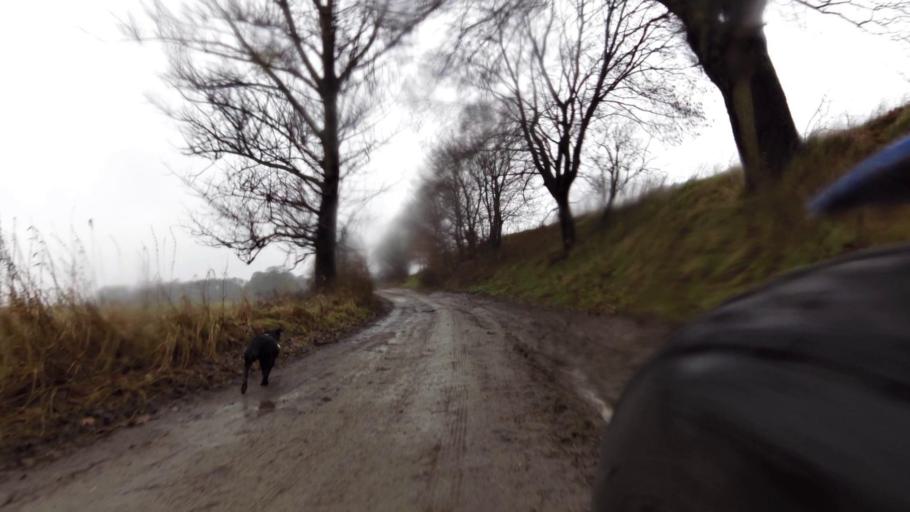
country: PL
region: West Pomeranian Voivodeship
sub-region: Powiat drawski
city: Zlocieniec
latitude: 53.5478
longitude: 15.9469
